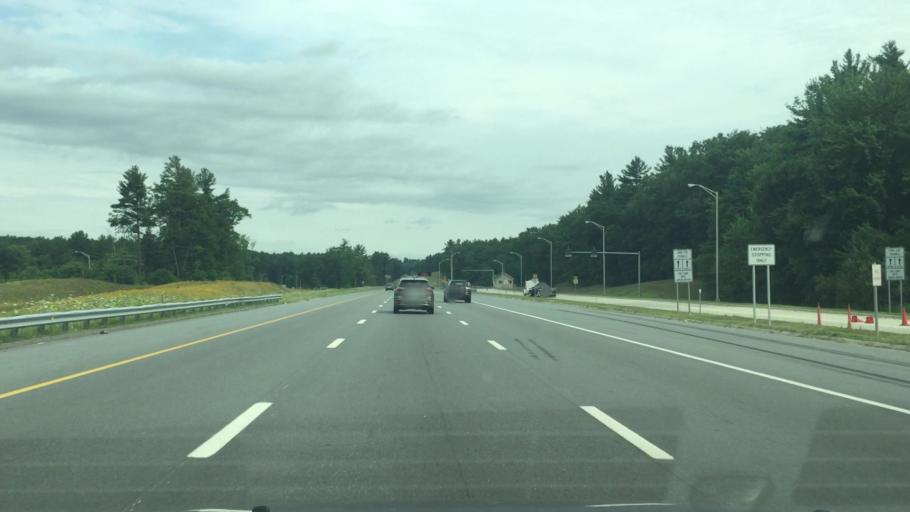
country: US
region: New Hampshire
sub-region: Rockingham County
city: Windham
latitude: 42.8211
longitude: -71.2875
